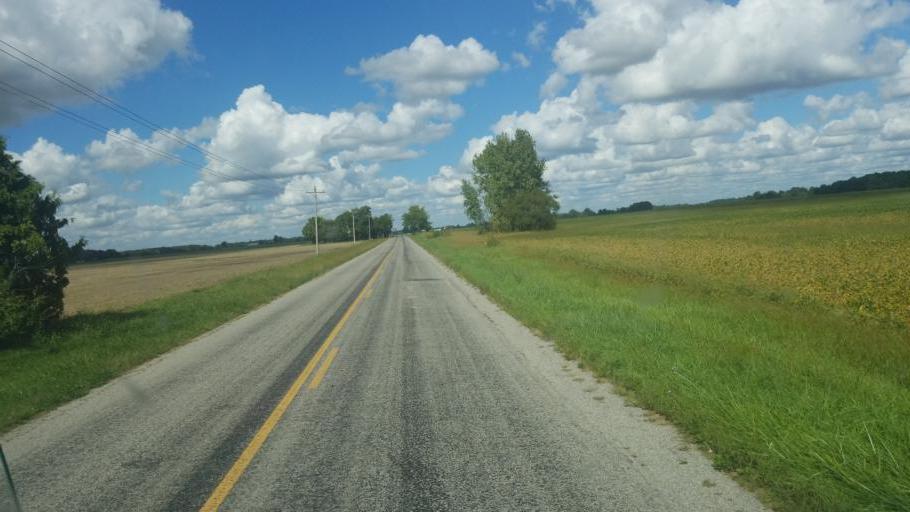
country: US
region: Ohio
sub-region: Champaign County
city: North Lewisburg
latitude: 40.3810
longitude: -83.5070
